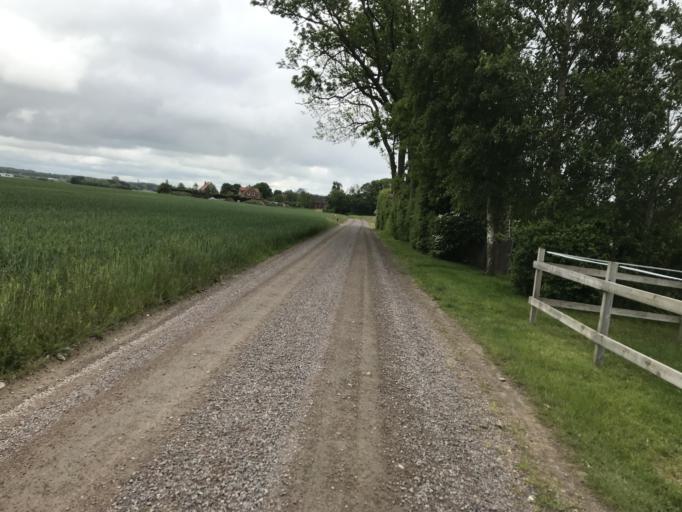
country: SE
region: Skane
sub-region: Landskrona
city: Asmundtorp
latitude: 55.8686
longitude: 12.9175
